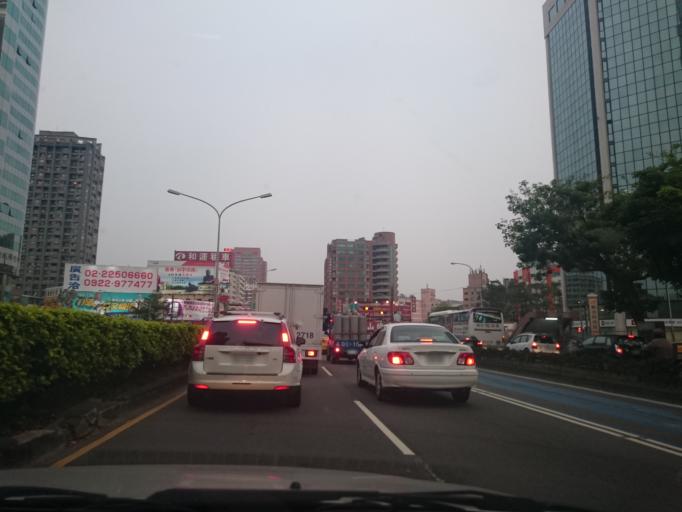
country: TW
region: Taiwan
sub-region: Taichung City
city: Taichung
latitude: 24.1514
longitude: 120.6686
